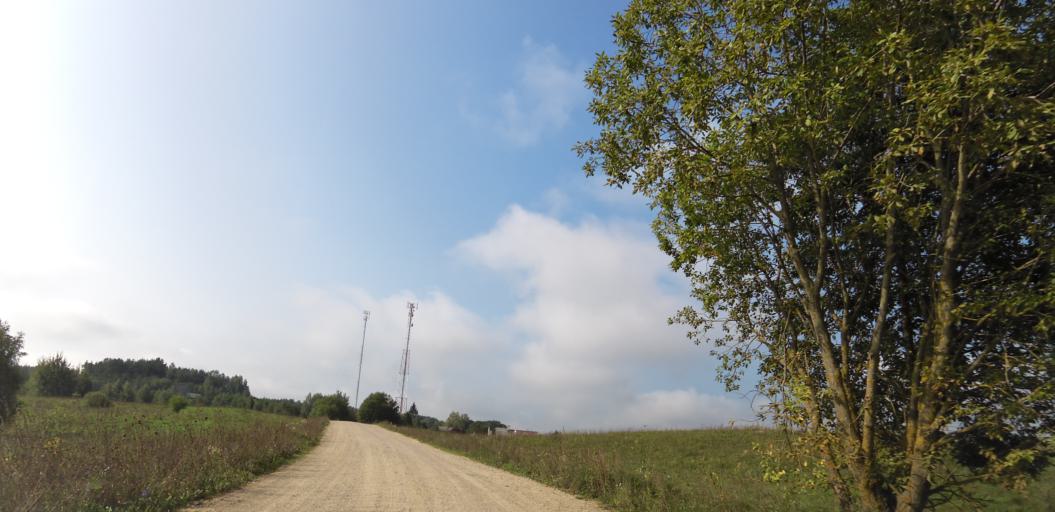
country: LT
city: Grigiskes
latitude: 54.7727
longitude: 25.0775
